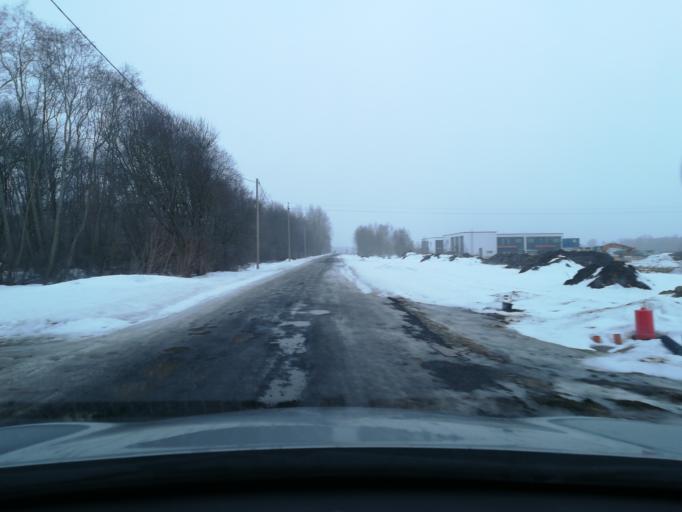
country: EE
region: Harju
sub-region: Rae vald
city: Jueri
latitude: 59.3753
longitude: 24.8679
